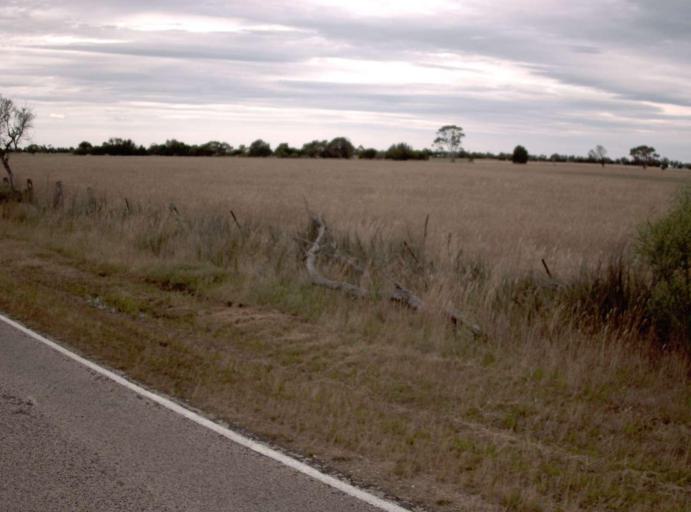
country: AU
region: Victoria
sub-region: East Gippsland
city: Bairnsdale
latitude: -37.9607
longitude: 147.4961
